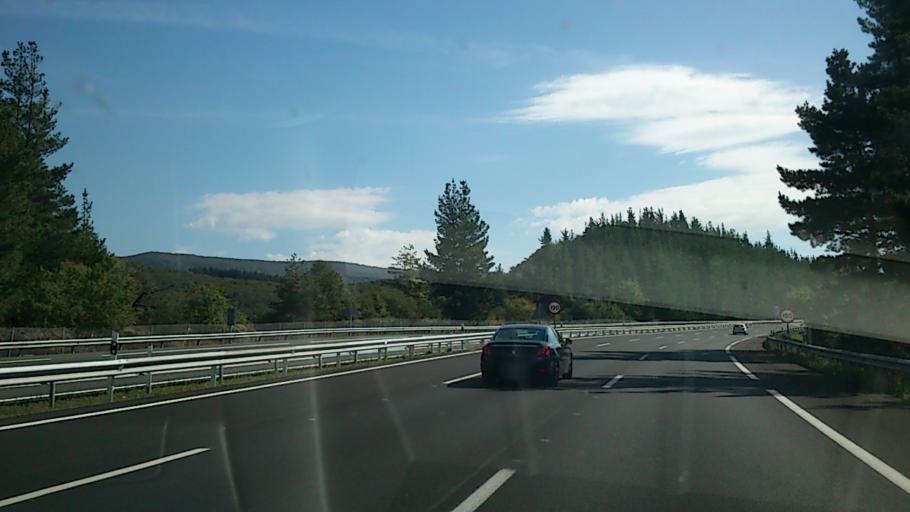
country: ES
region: Basque Country
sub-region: Provincia de Alava
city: Lezama
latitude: 43.0083
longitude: -2.8999
